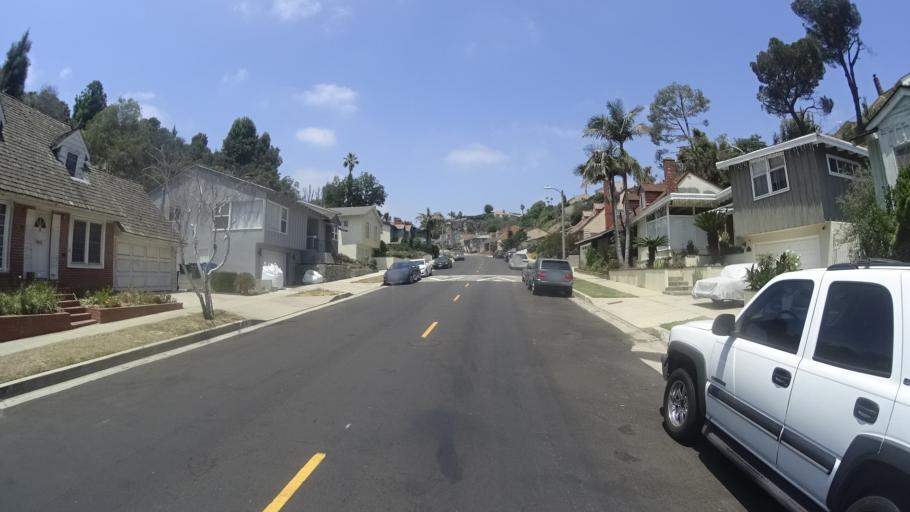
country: US
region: California
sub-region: Los Angeles County
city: View Park-Windsor Hills
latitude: 34.0072
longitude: -118.3455
